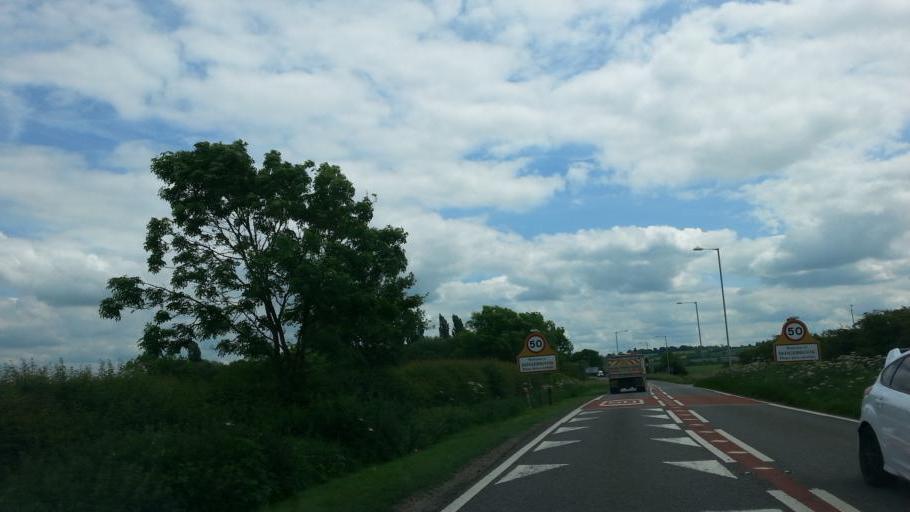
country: GB
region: England
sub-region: Lincolnshire
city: Barrowby
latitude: 52.9305
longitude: -0.7340
